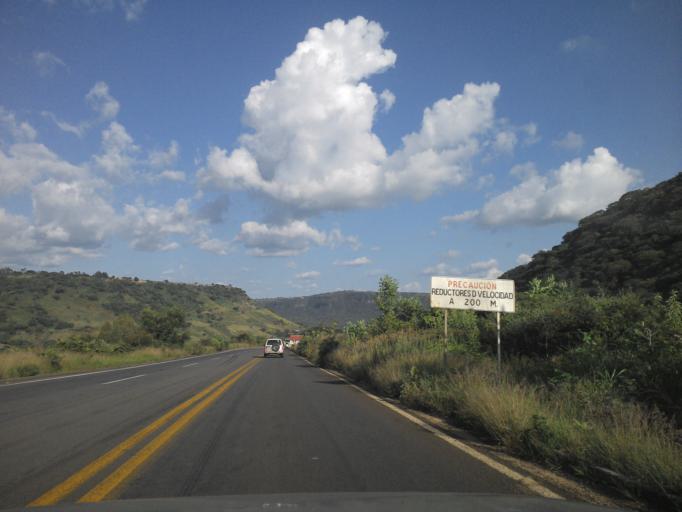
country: MX
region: Jalisco
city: Atotonilco el Alto
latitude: 20.5660
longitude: -102.5205
